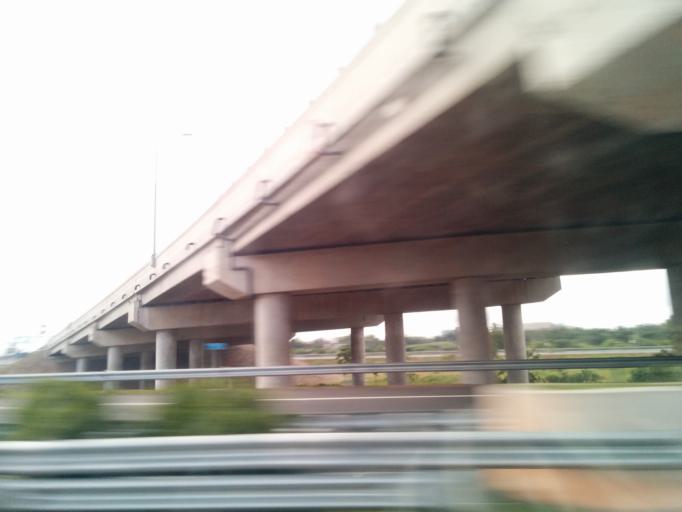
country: LK
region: Western
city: Peliyagoda
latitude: 6.9682
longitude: 79.8932
